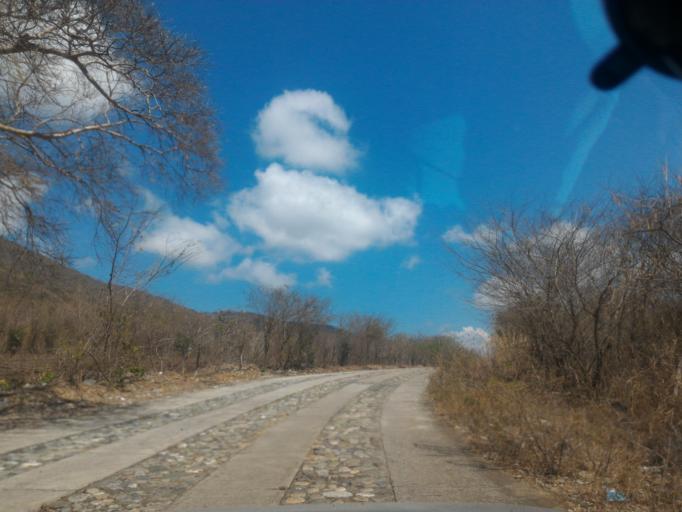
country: MX
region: Michoacan
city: Coahuayana Viejo
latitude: 18.5606
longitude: -103.6379
